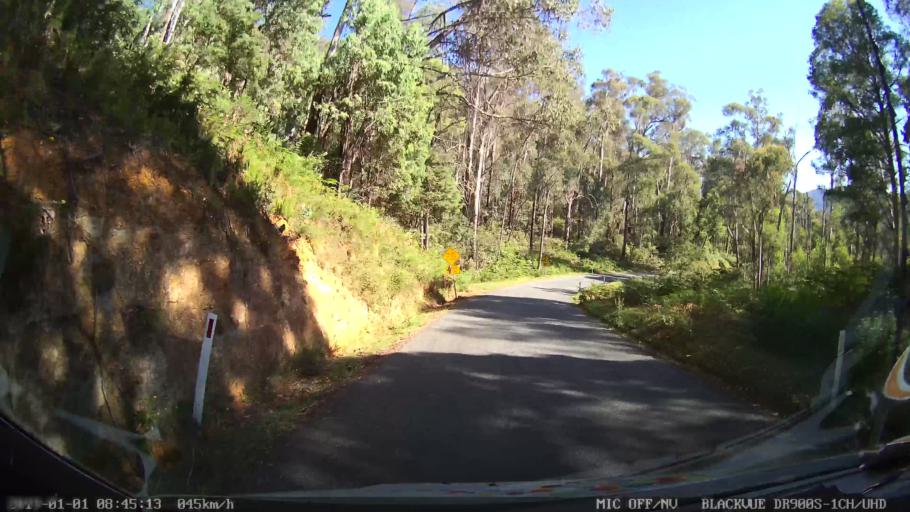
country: AU
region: New South Wales
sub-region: Snowy River
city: Jindabyne
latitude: -36.3068
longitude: 148.1877
